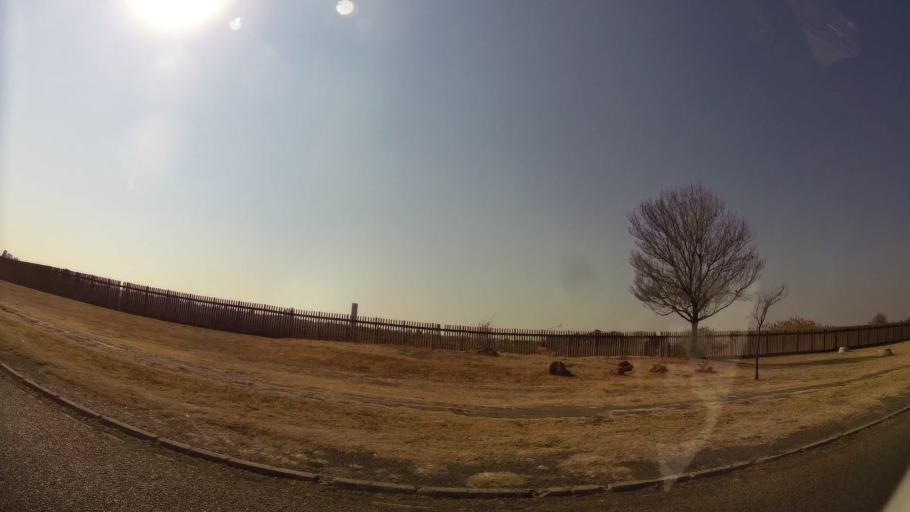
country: ZA
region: Gauteng
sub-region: Ekurhuleni Metropolitan Municipality
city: Boksburg
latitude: -26.2385
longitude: 28.2611
